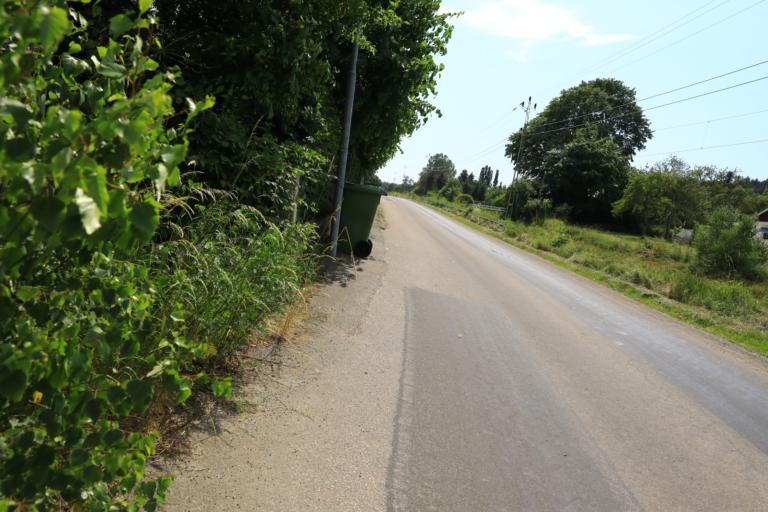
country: SE
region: Halland
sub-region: Varbergs Kommun
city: Varberg
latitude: 57.1732
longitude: 12.3005
